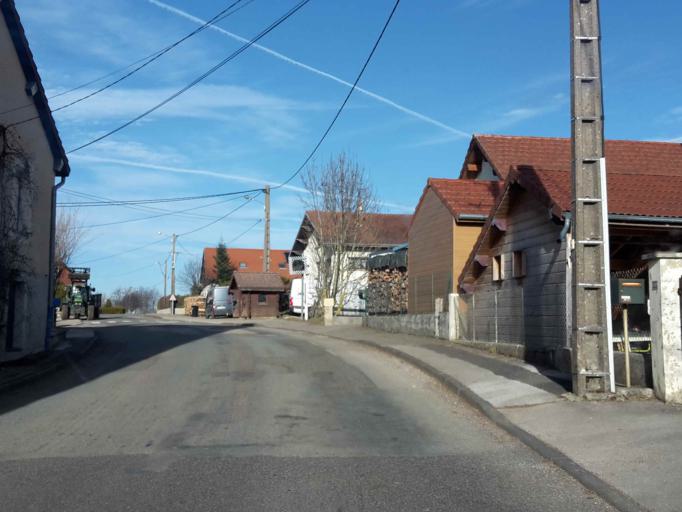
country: FR
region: Franche-Comte
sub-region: Departement du Doubs
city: Vercel-Villedieu-le-Camp
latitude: 47.1684
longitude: 6.3923
